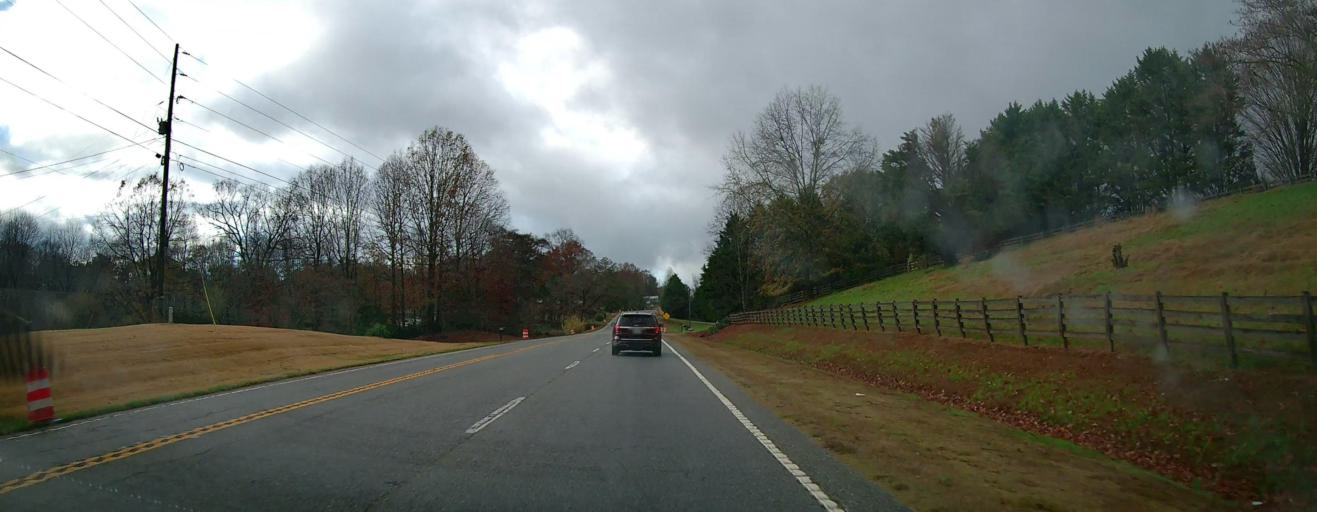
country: US
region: Georgia
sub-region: Habersham County
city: Demorest
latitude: 34.5474
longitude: -83.6291
